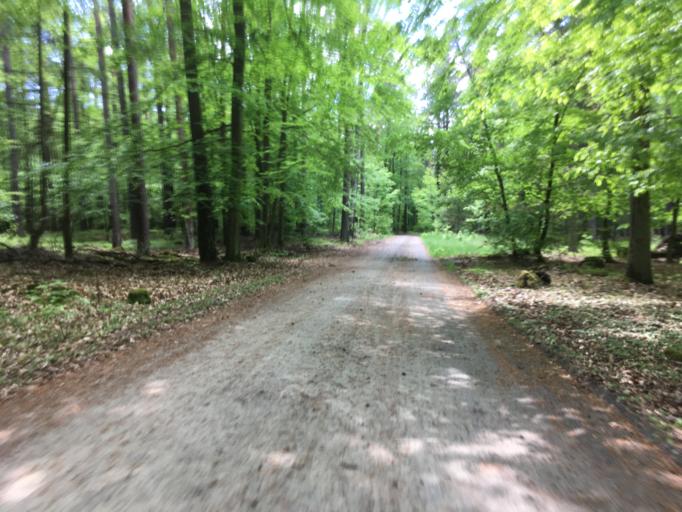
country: DE
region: Brandenburg
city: Marienwerder
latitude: 52.8236
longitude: 13.6275
